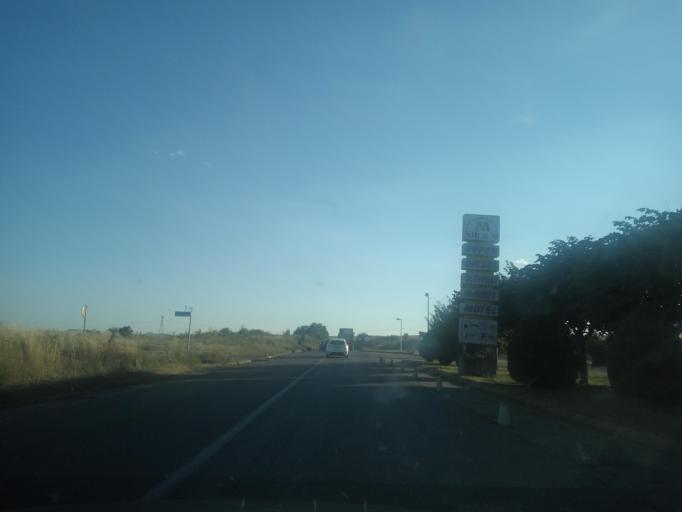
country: XK
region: Gjakova
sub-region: Komuna e Gjakoves
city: Gjakove
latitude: 42.4529
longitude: 20.5012
